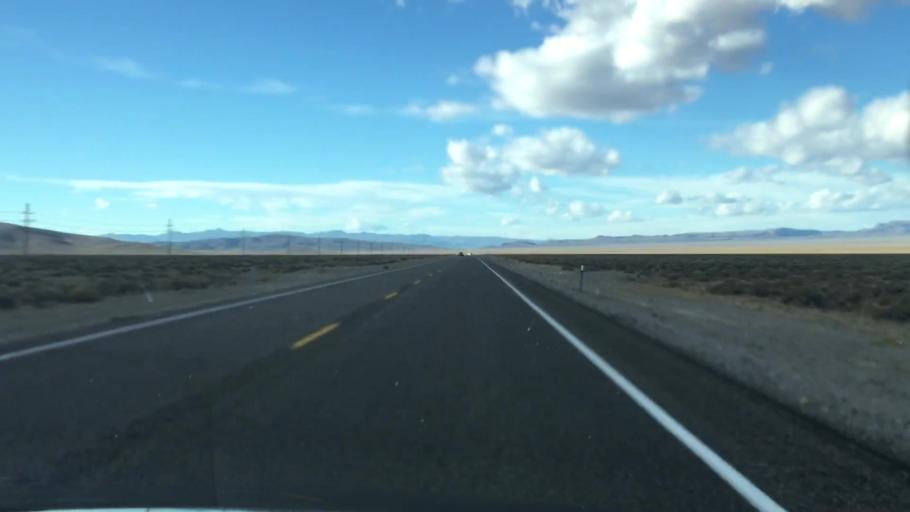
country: US
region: Nevada
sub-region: Nye County
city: Beatty
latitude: 37.1196
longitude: -116.8213
